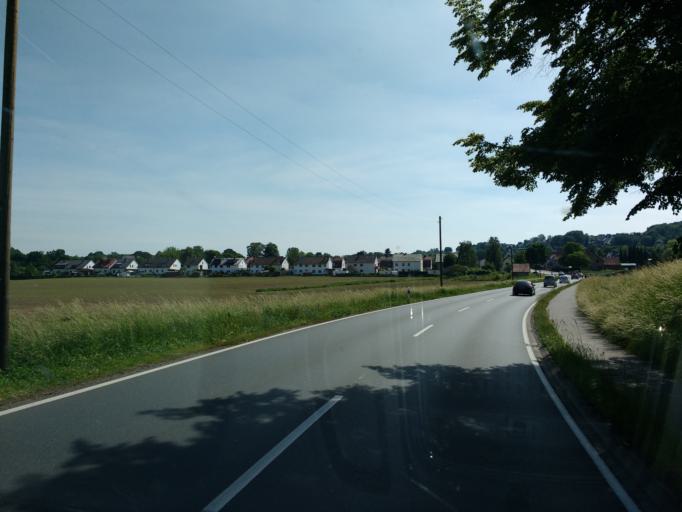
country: DE
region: North Rhine-Westphalia
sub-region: Regierungsbezirk Detmold
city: Herford
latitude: 52.1528
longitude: 8.6742
